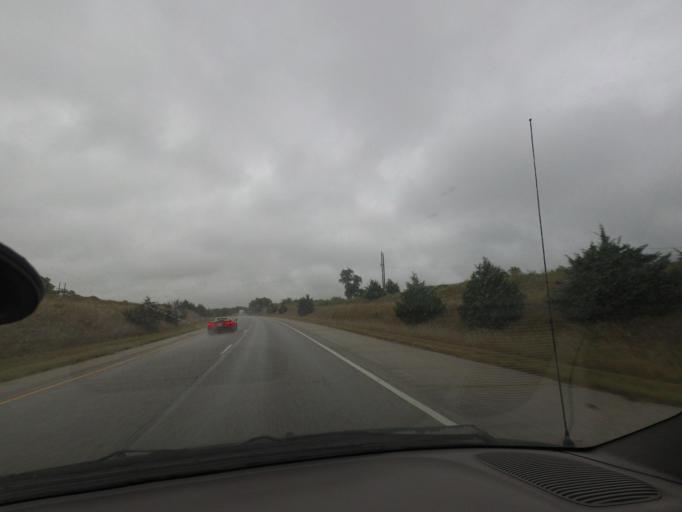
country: US
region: Illinois
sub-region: Pike County
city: Barry
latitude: 39.7288
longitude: -91.1225
